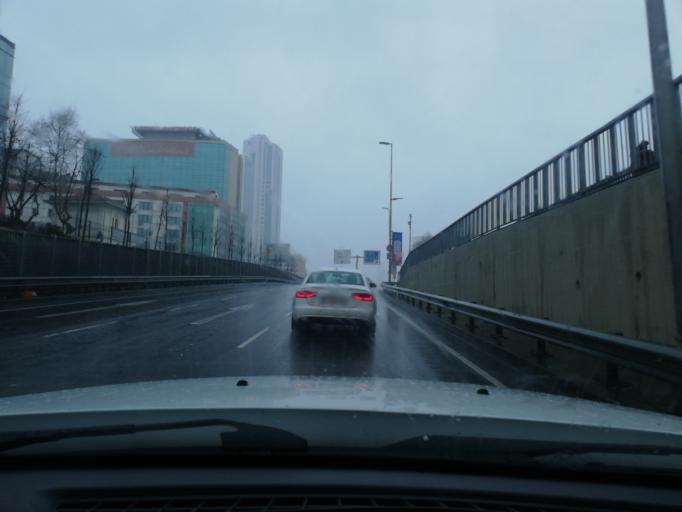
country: TR
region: Istanbul
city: Sisli
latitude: 41.0699
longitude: 28.9813
